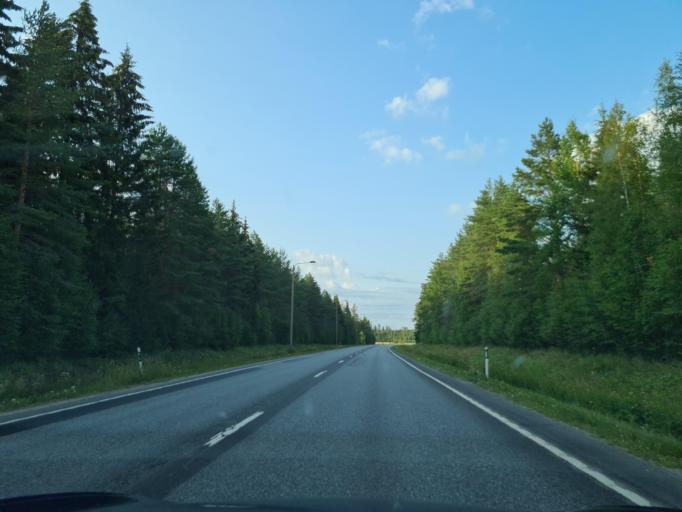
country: FI
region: Southern Ostrobothnia
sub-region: Seinaejoki
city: Kauhava
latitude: 63.0652
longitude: 23.0441
